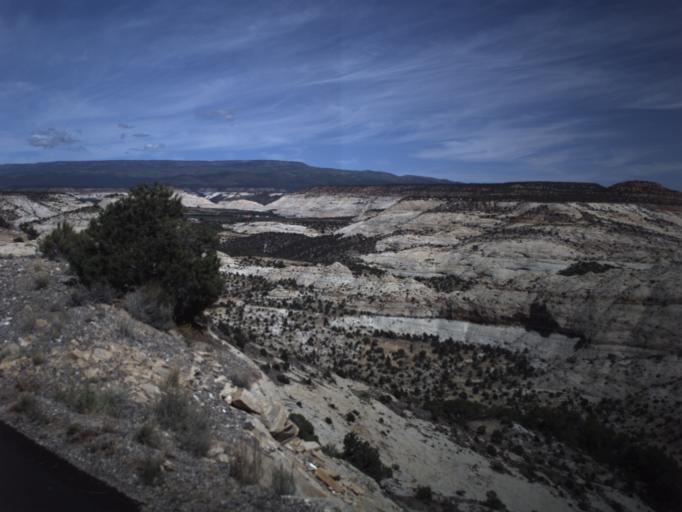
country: US
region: Utah
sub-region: Wayne County
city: Loa
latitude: 37.8313
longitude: -111.4151
